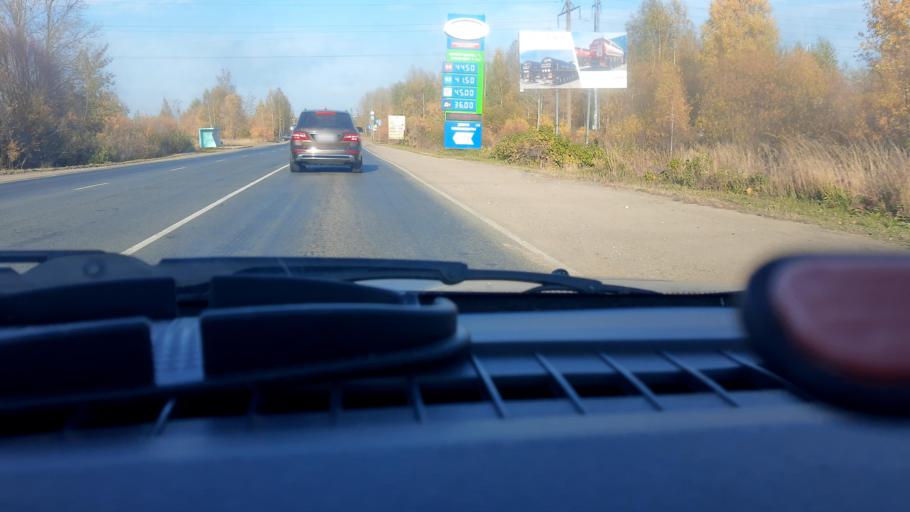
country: RU
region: Nizjnij Novgorod
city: Kstovo
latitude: 56.1153
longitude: 44.1509
